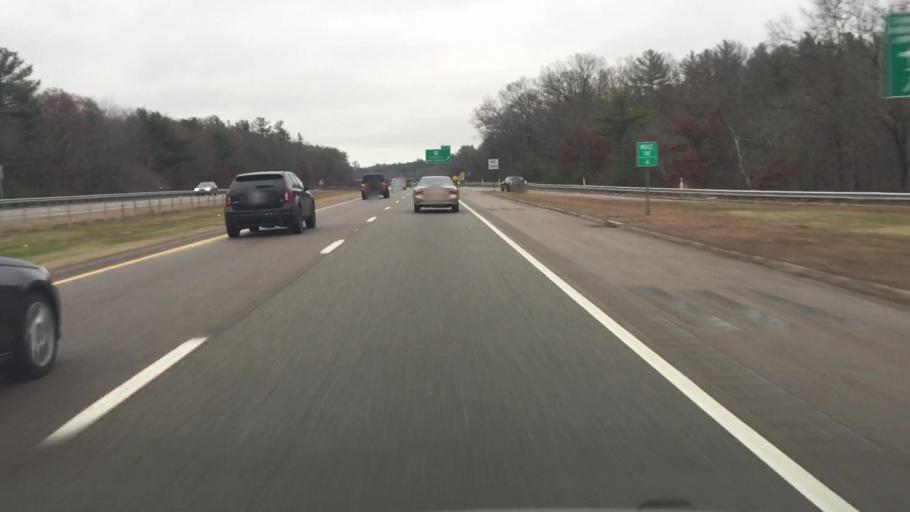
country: US
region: Massachusetts
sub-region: Plymouth County
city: Middleborough Center
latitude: 41.9013
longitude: -70.9631
